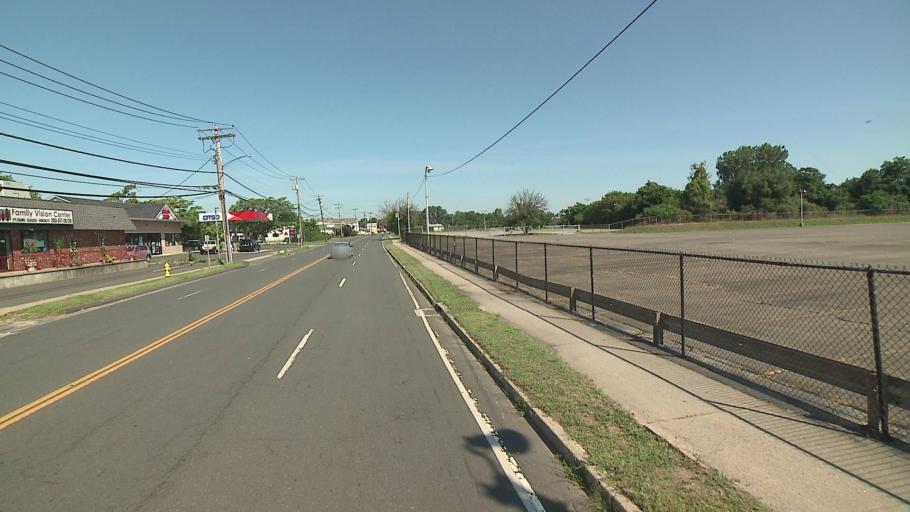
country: US
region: Connecticut
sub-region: Fairfield County
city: Stratford
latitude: 41.1723
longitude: -73.1280
